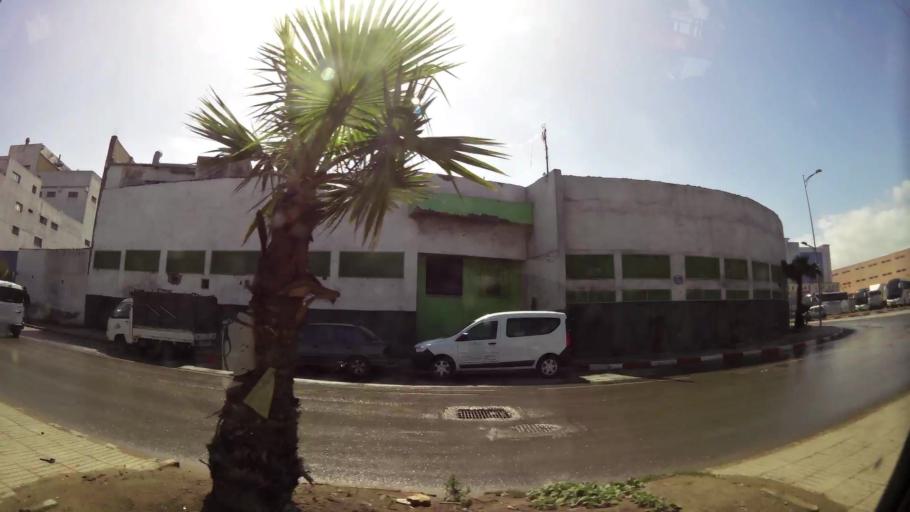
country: MA
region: Grand Casablanca
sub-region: Mediouna
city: Tit Mellil
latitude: 33.6242
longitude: -7.5064
